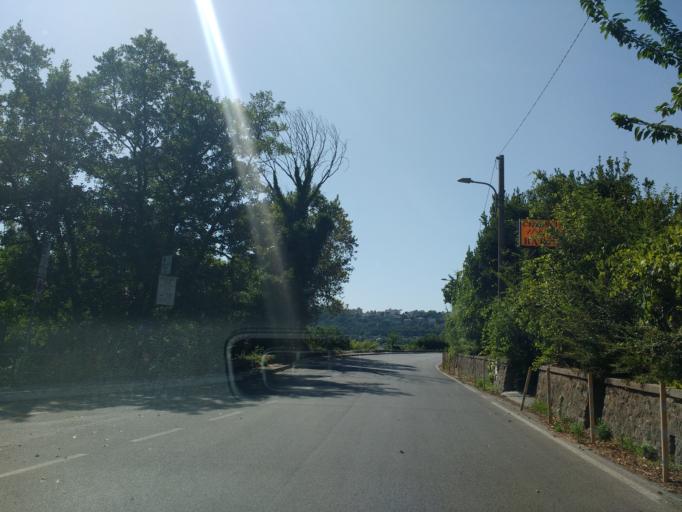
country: IT
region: Latium
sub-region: Citta metropolitana di Roma Capitale
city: Castel Gandolfo
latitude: 41.7592
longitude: 12.6684
